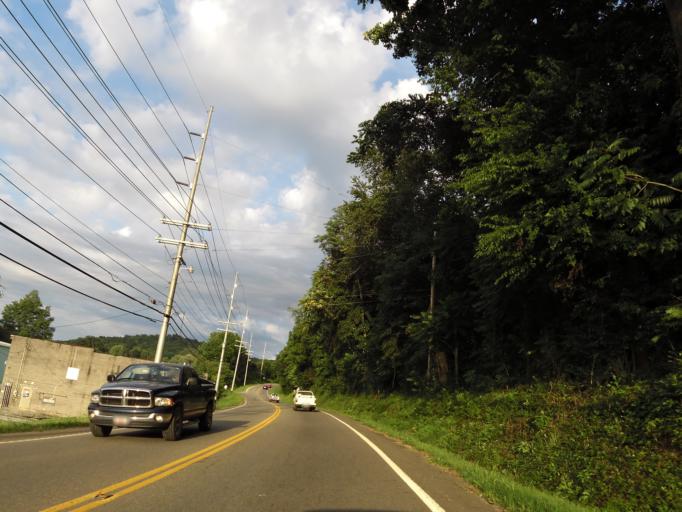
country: US
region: Tennessee
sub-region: Cocke County
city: Newport
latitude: 35.9567
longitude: -83.1669
